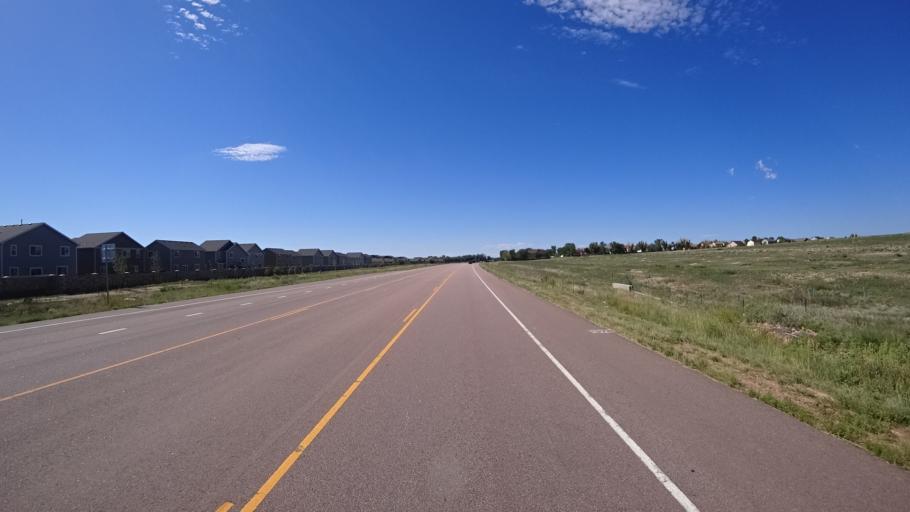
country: US
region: Colorado
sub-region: El Paso County
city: Security-Widefield
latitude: 38.7438
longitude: -104.6482
